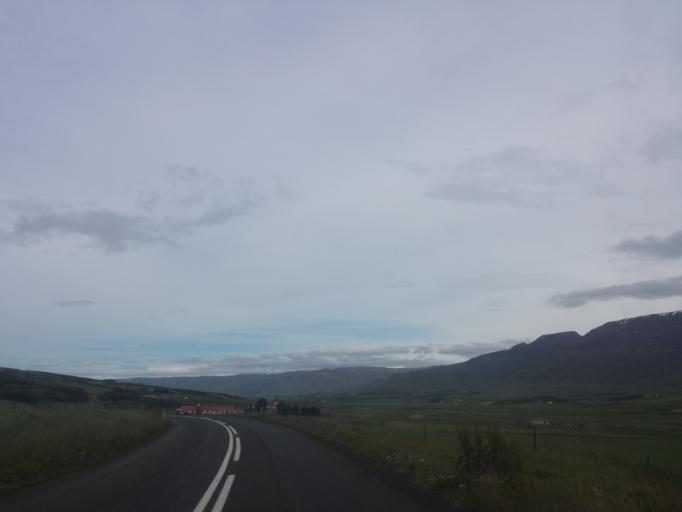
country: IS
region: Northeast
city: Akureyri
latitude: 65.5141
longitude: -18.1619
